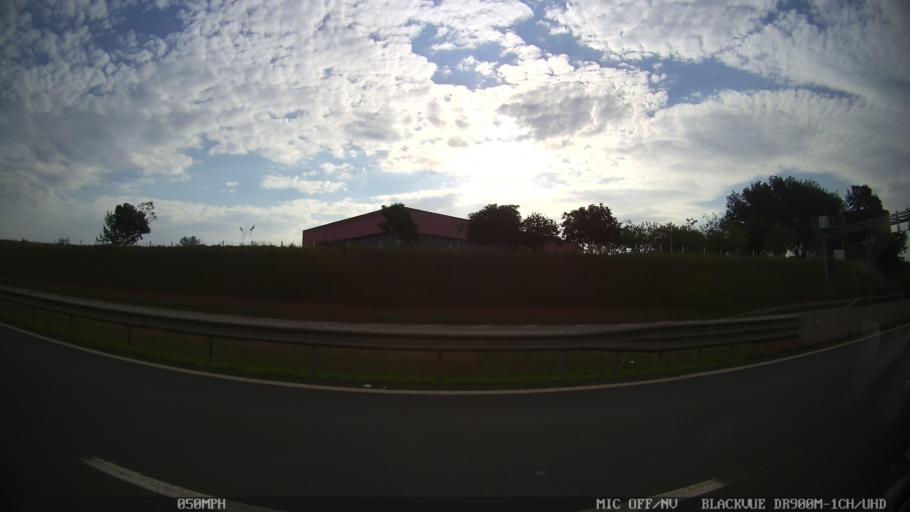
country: BR
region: Sao Paulo
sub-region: Cosmopolis
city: Cosmopolis
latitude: -22.6208
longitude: -47.1997
